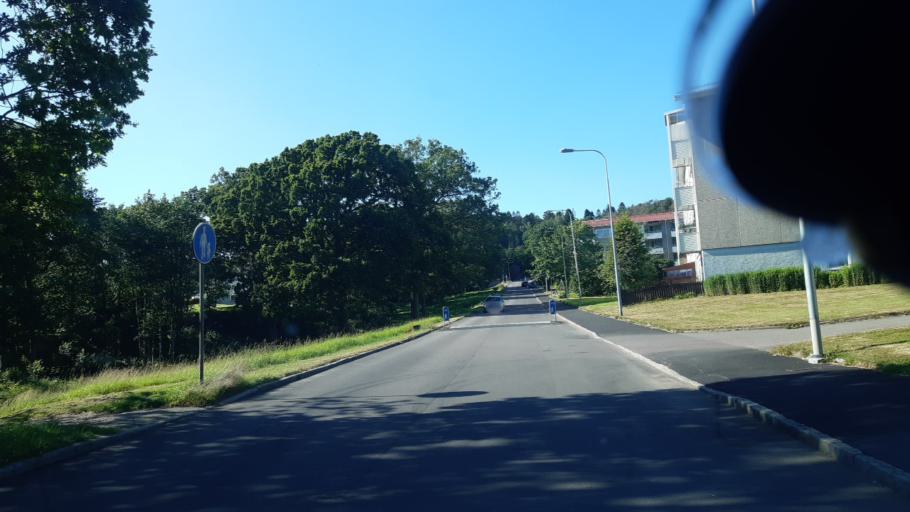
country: SE
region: Vaestra Goetaland
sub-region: Goteborg
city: Eriksbo
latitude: 57.7693
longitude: 12.0346
